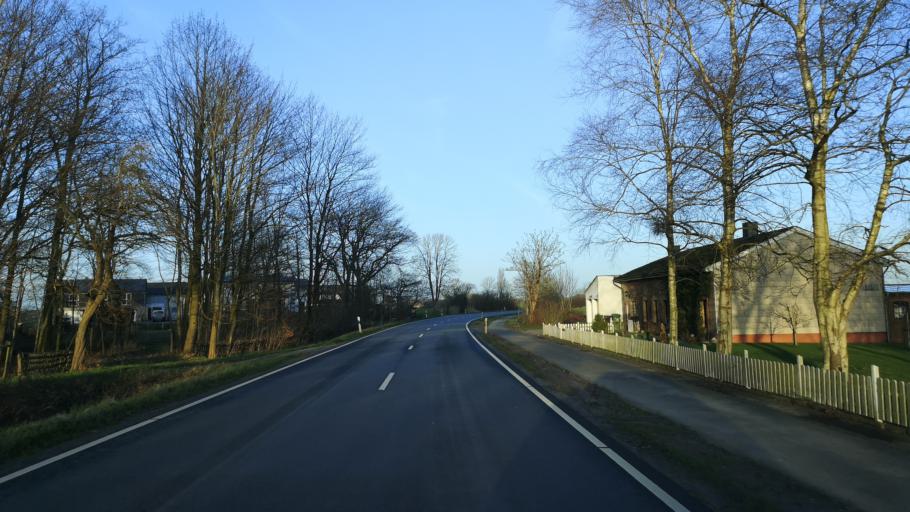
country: DE
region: Schleswig-Holstein
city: Grosssolt
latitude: 54.6912
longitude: 9.4962
